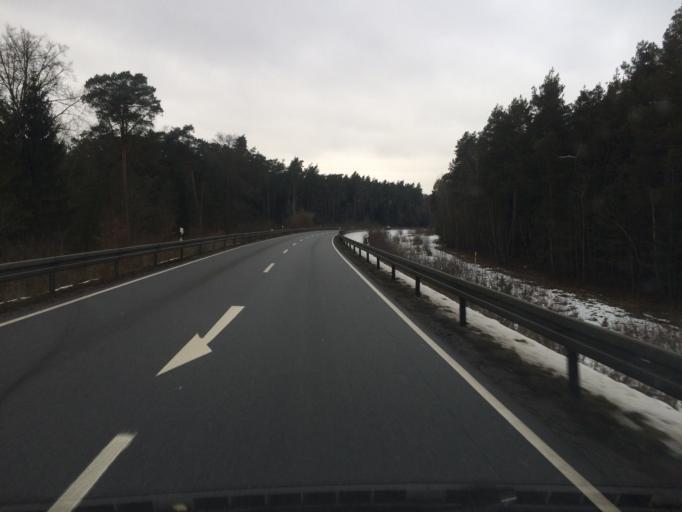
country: DE
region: Bavaria
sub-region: Upper Palatinate
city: Teublitz
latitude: 49.2184
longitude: 12.1215
